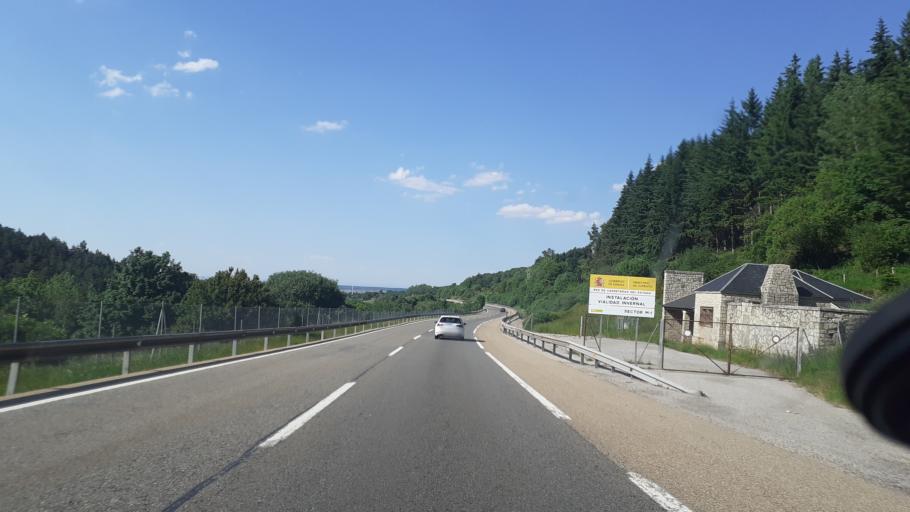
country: ES
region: Madrid
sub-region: Provincia de Madrid
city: Somosierra
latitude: 41.1641
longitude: -3.5816
